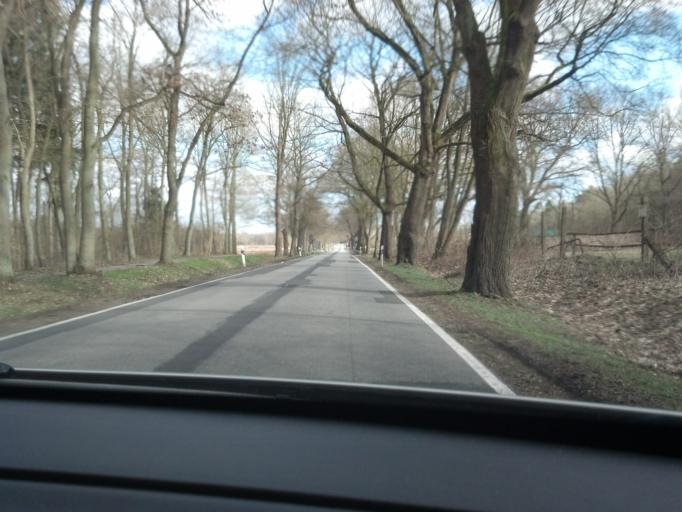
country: DE
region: Mecklenburg-Vorpommern
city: Boizenburg
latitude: 53.4113
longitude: 10.7411
